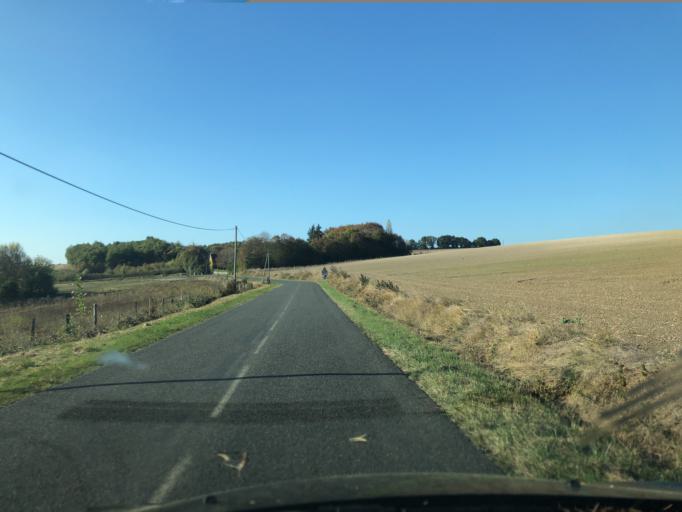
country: FR
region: Centre
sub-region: Departement d'Indre-et-Loire
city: Neuvy-le-Roi
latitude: 47.6662
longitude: 0.6330
